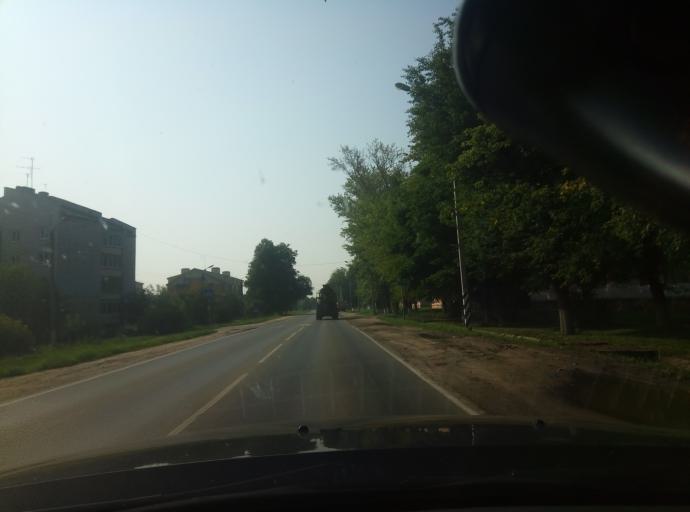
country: RU
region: Kaluga
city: Belousovo
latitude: 55.0915
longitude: 36.6657
